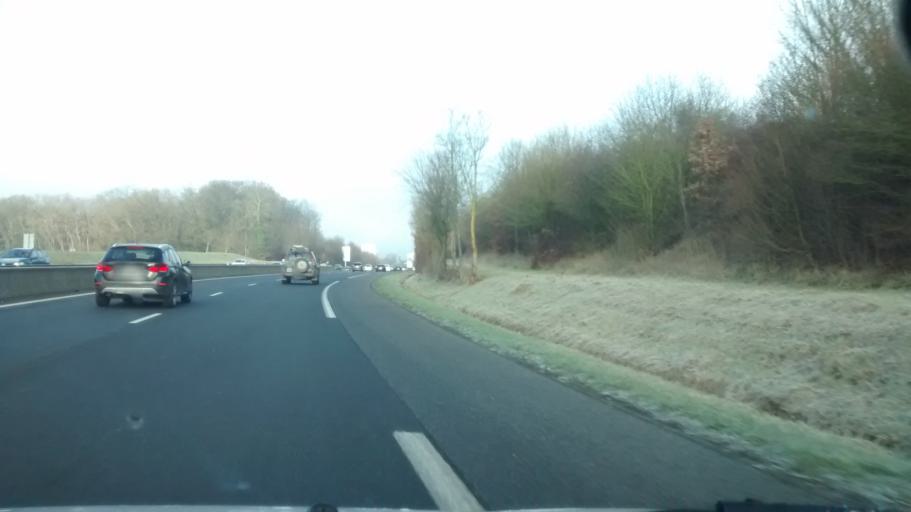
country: FR
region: Centre
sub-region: Departement d'Indre-et-Loire
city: Joue-les-Tours
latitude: 47.3321
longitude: 0.6739
